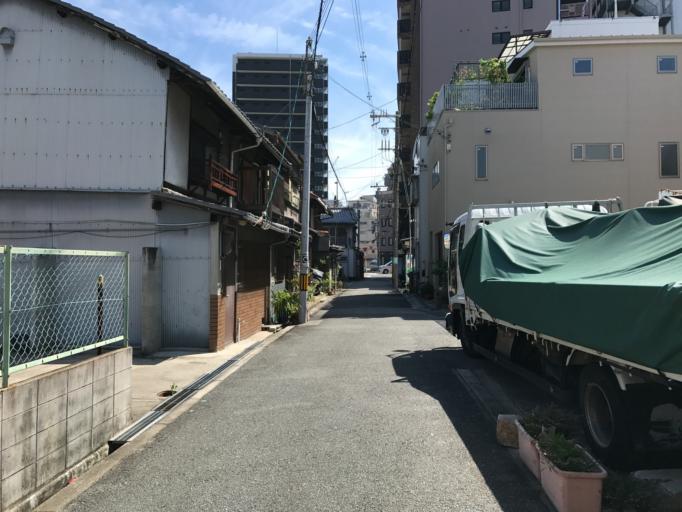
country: JP
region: Osaka
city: Osaka-shi
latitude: 34.6957
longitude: 135.4719
